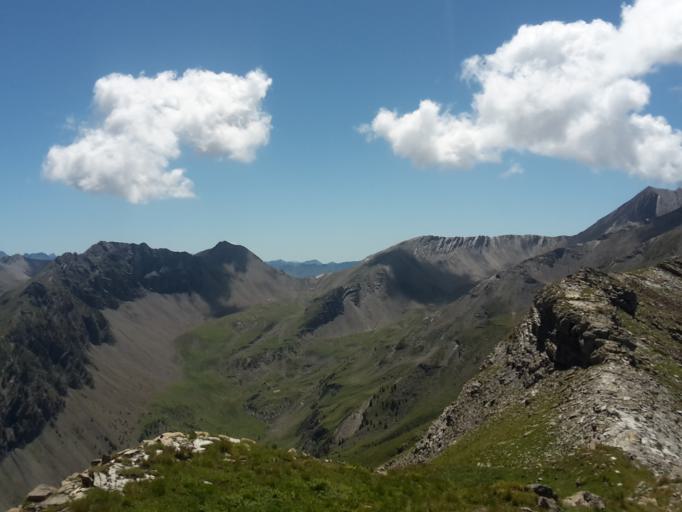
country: FR
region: Provence-Alpes-Cote d'Azur
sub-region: Departement des Hautes-Alpes
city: Embrun
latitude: 44.6557
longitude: 6.4206
